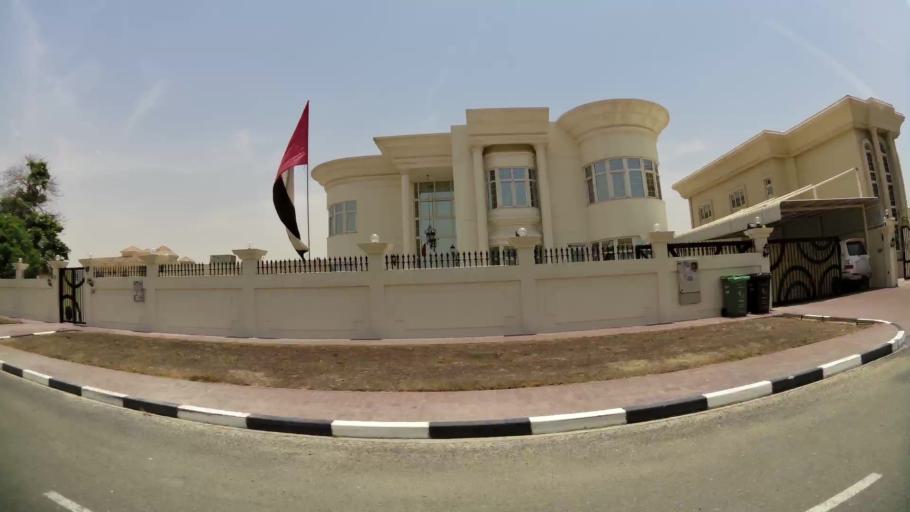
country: AE
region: Ash Shariqah
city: Sharjah
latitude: 25.2015
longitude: 55.3828
